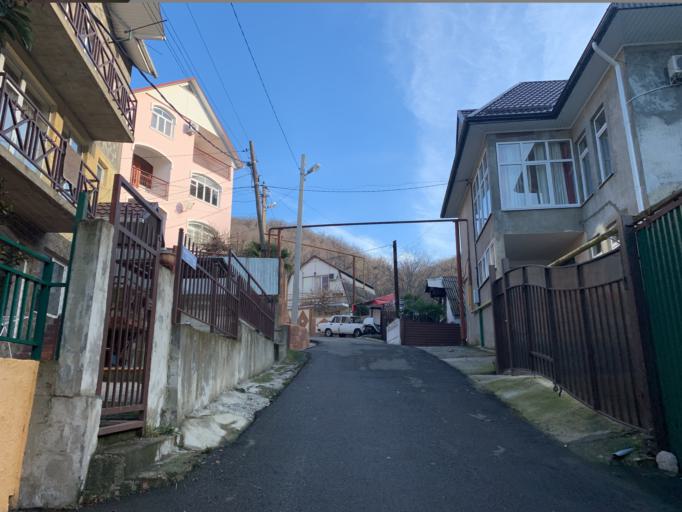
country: RU
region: Krasnodarskiy
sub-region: Sochi City
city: Lazarevskoye
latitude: 43.9225
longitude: 39.3233
